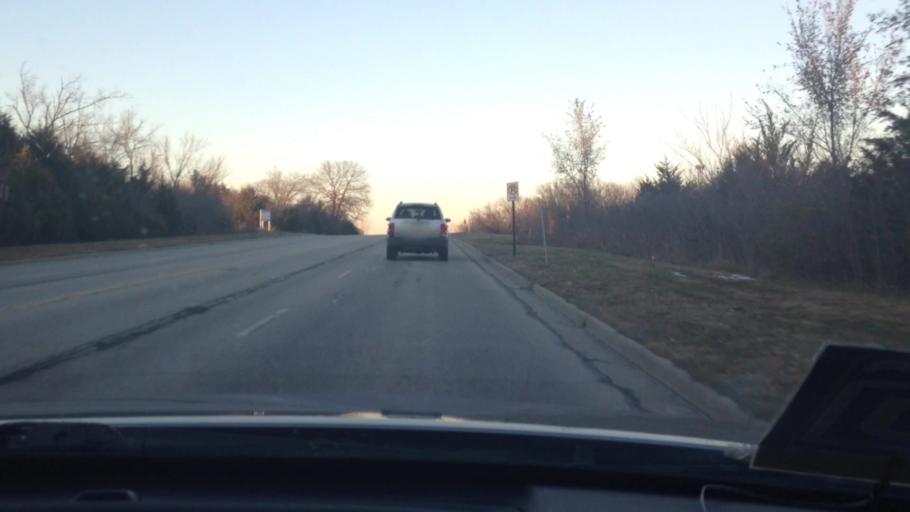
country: US
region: Kansas
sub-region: Wyandotte County
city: Bonner Springs
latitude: 39.1090
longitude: -94.8815
